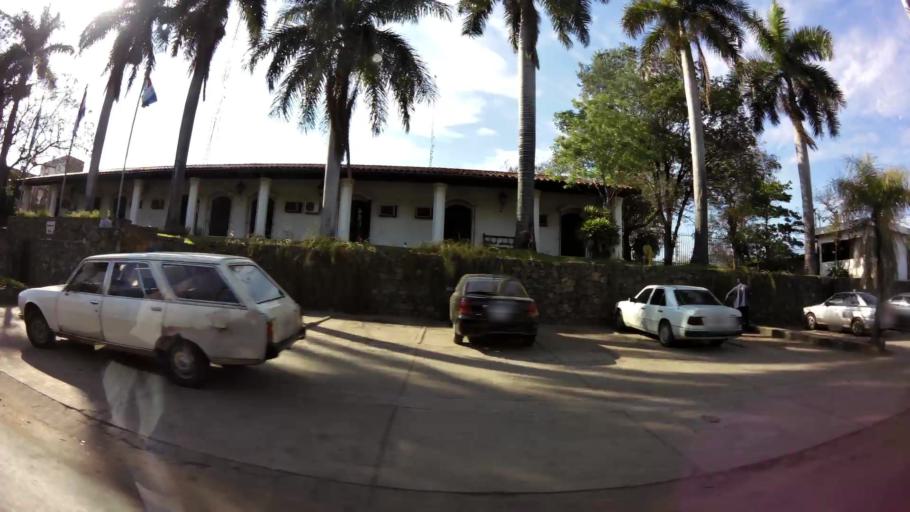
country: PY
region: Asuncion
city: Asuncion
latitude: -25.2726
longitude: -57.6058
